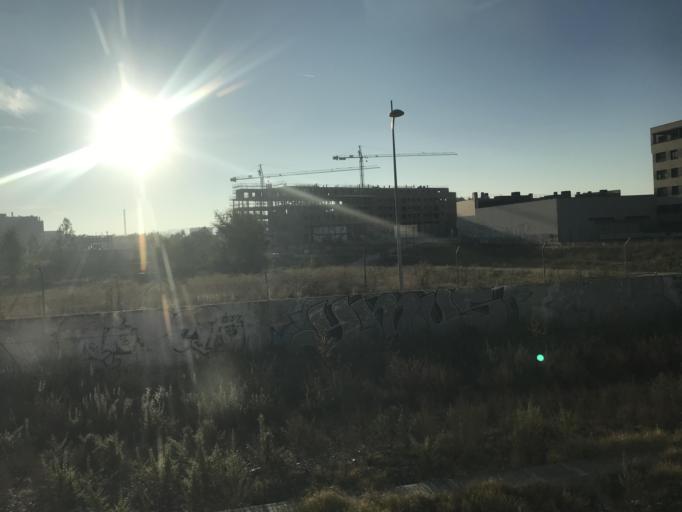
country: ES
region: Castille and Leon
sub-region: Provincia de Valladolid
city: Valladolid
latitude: 41.6569
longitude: -4.7064
